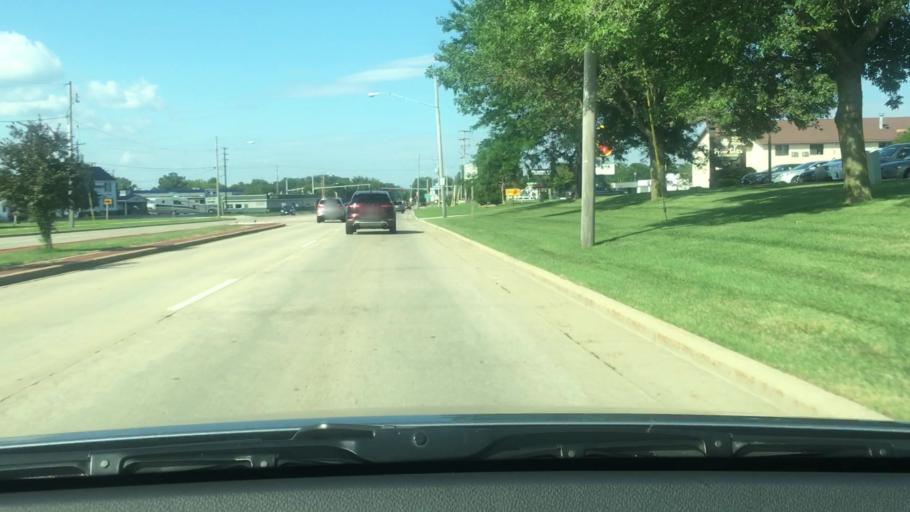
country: US
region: Wisconsin
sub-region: Winnebago County
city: Oshkosh
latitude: 43.9941
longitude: -88.5764
